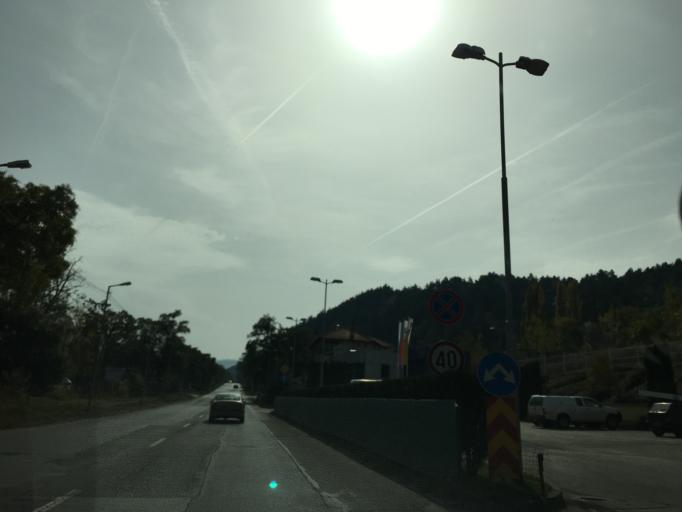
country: BG
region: Sofia-Capital
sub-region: Stolichna Obshtina
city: Sofia
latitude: 42.6087
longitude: 23.3998
